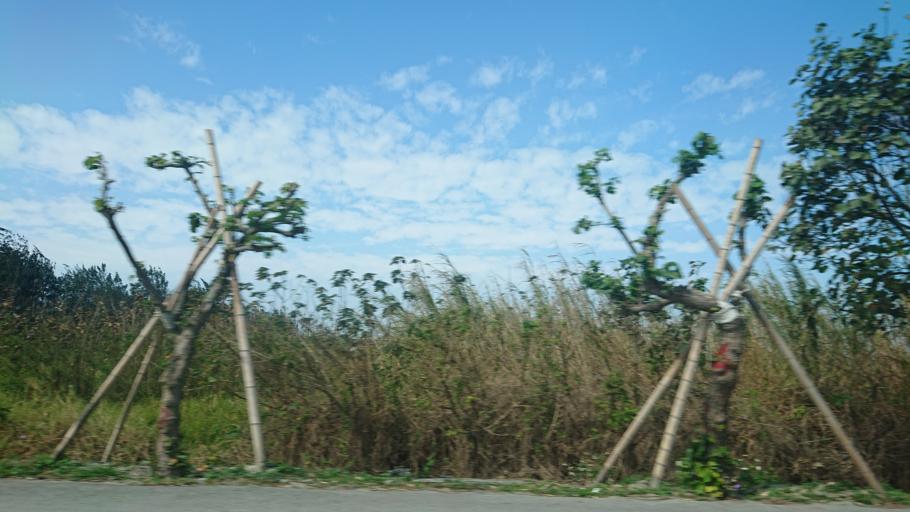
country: TW
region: Taiwan
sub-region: Changhua
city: Chang-hua
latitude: 23.9066
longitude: 120.3086
